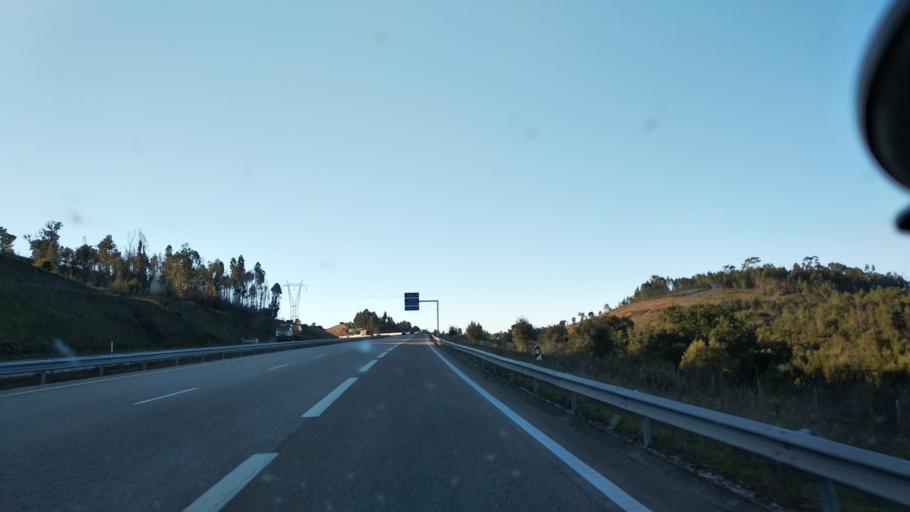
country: PT
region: Santarem
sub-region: Abrantes
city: Alferrarede
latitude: 39.4940
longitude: -8.0713
